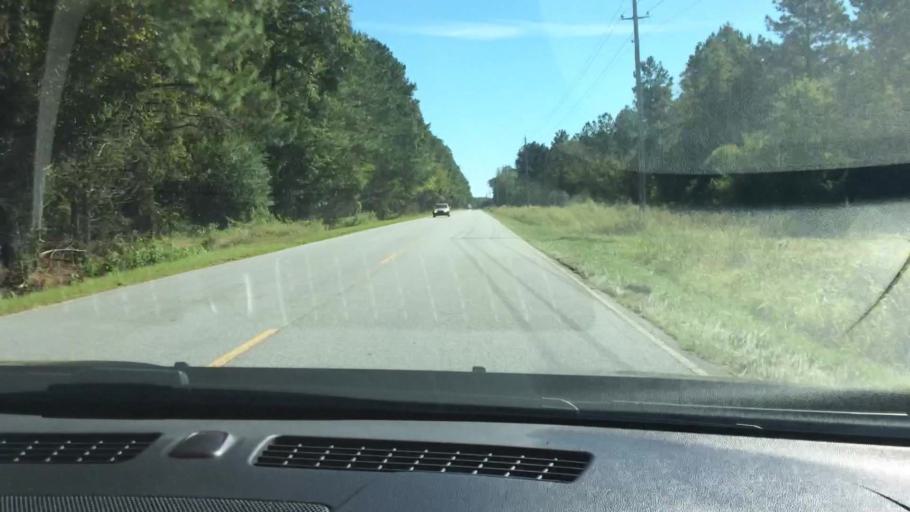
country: US
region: North Carolina
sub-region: Pitt County
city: Grifton
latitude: 35.3997
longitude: -77.4070
